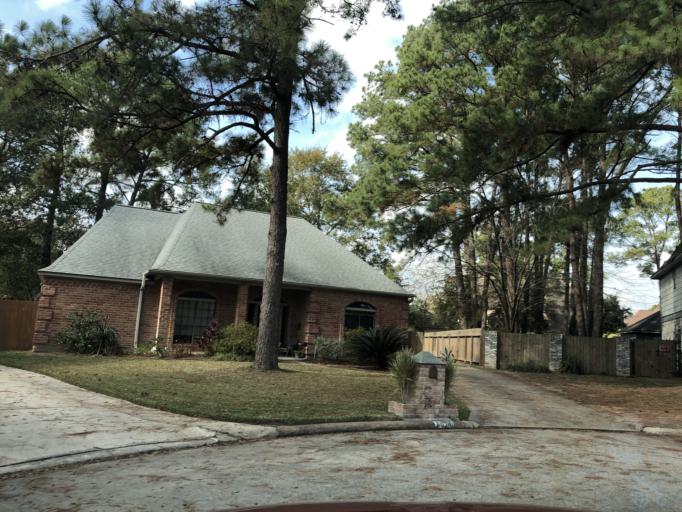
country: US
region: Texas
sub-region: Harris County
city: Tomball
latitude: 30.0297
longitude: -95.5467
